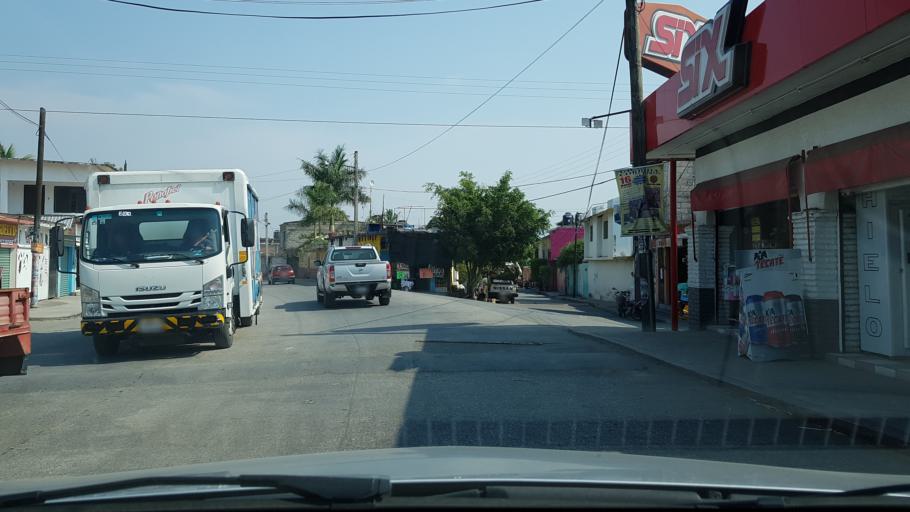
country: MX
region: Morelos
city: Zacatepec
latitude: 18.6633
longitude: -99.1858
